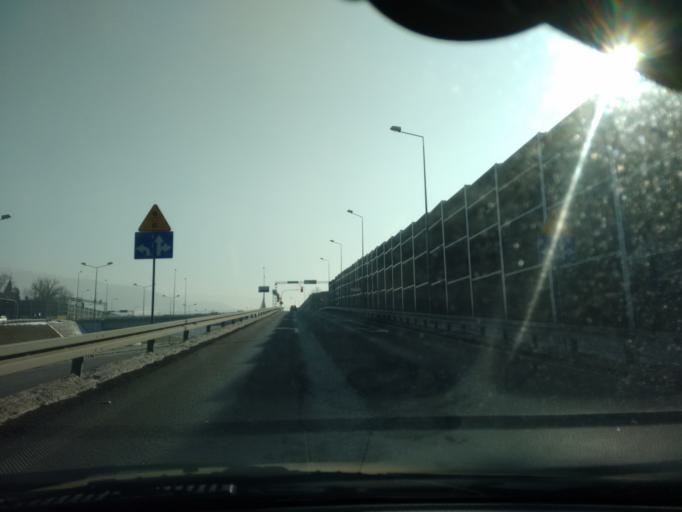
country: PL
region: Silesian Voivodeship
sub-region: Bielsko-Biala
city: Bielsko-Biala
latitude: 49.8248
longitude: 19.0856
